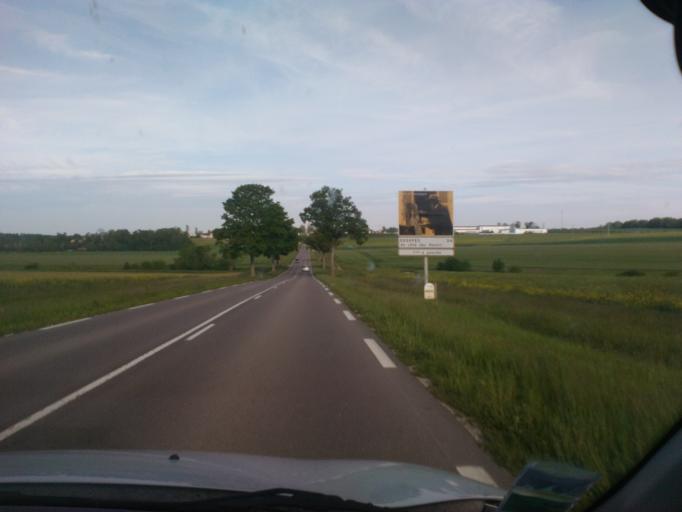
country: FR
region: Champagne-Ardenne
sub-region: Departement de l'Aube
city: Vendeuvre-sur-Barse
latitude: 48.2377
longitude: 4.4938
